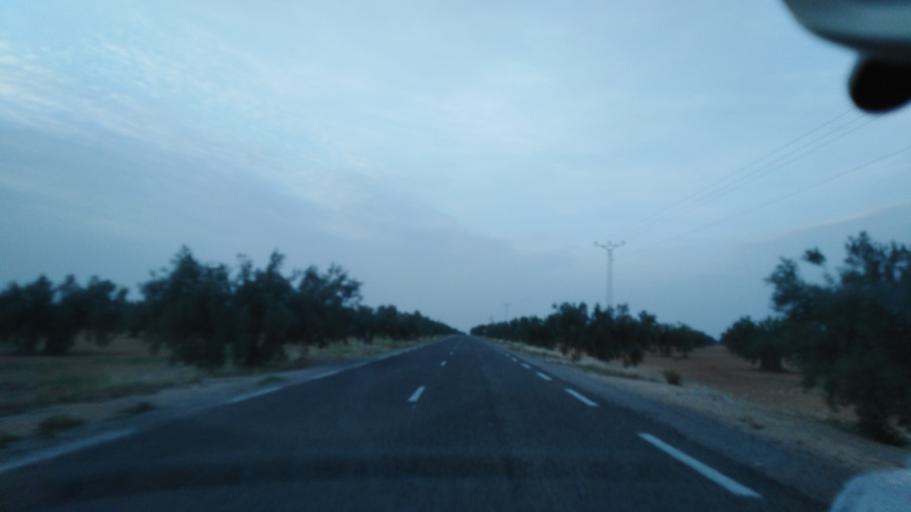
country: TN
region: Safaqis
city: Bi'r `Ali Bin Khalifah
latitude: 34.9080
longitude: 10.3877
